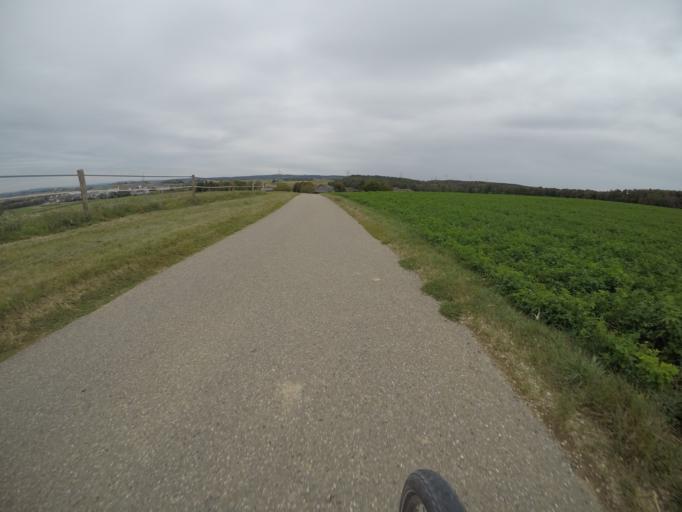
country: DE
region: Baden-Wuerttemberg
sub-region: Regierungsbezirk Stuttgart
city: Eberdingen
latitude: 48.8404
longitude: 8.9869
